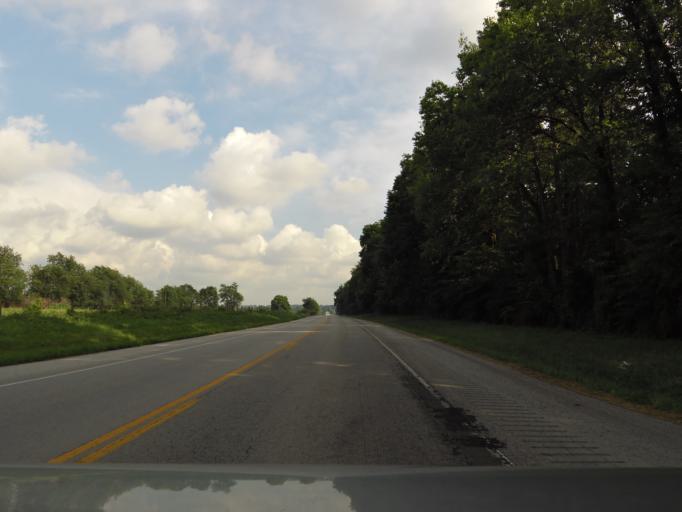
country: US
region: Kentucky
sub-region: Bourbon County
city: Paris
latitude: 38.2730
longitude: -84.2991
